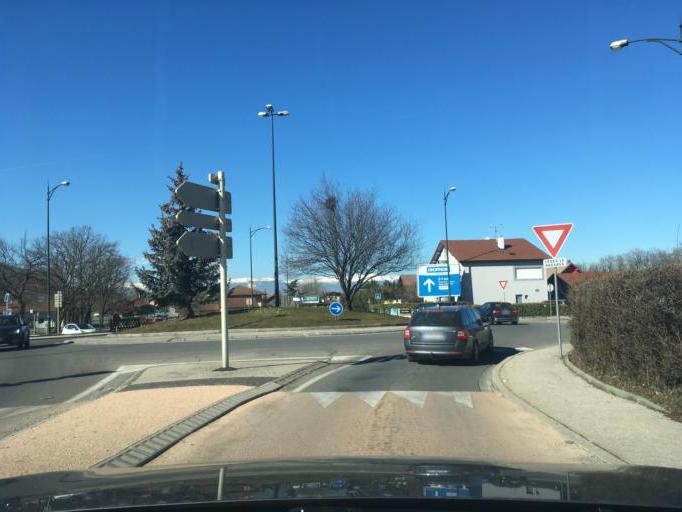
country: FR
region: Rhone-Alpes
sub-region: Departement de la Haute-Savoie
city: Vetraz-Monthoux
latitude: 46.1873
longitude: 6.2718
